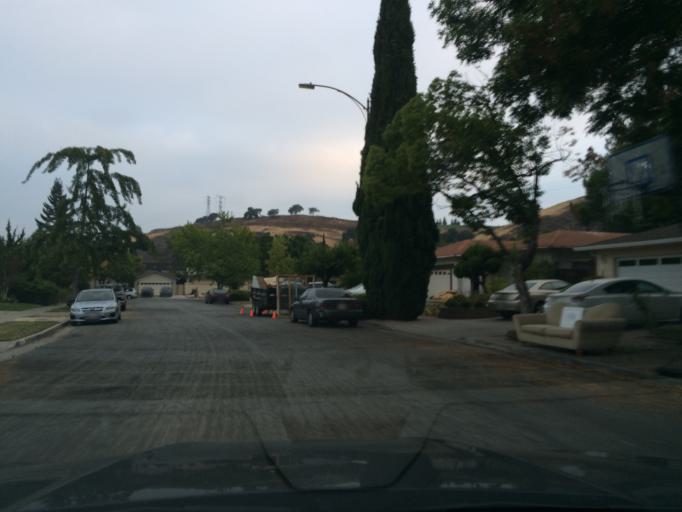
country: US
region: California
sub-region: Santa Clara County
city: Seven Trees
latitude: 37.2260
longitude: -121.8611
